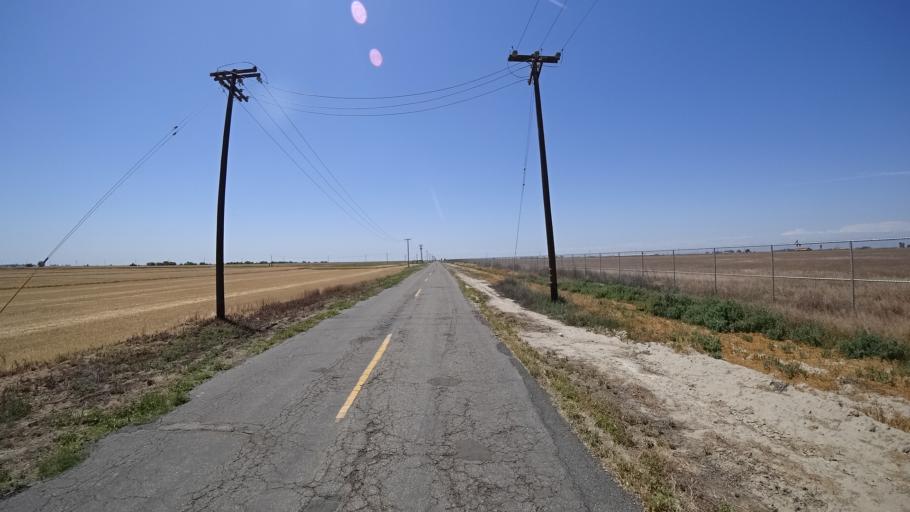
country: US
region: California
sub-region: Kings County
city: Lemoore
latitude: 36.2317
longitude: -119.7446
